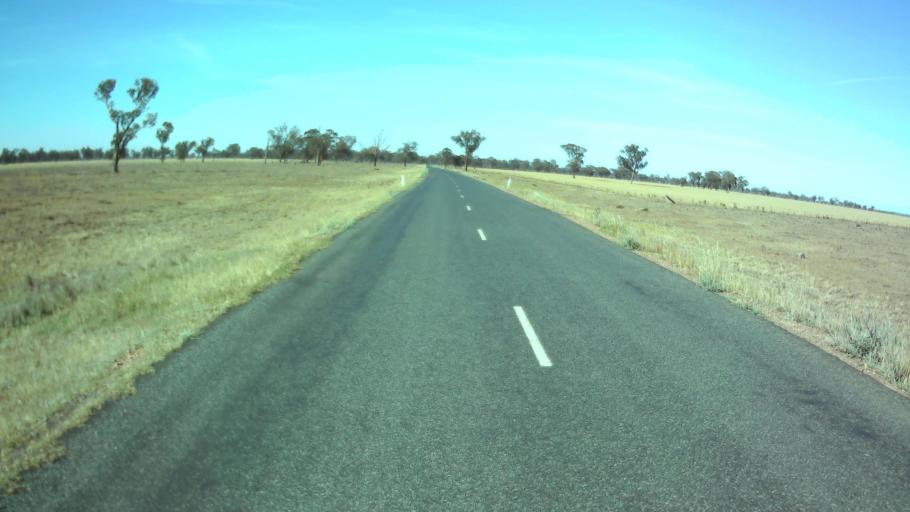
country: AU
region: New South Wales
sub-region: Weddin
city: Grenfell
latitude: -34.0505
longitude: 147.9198
